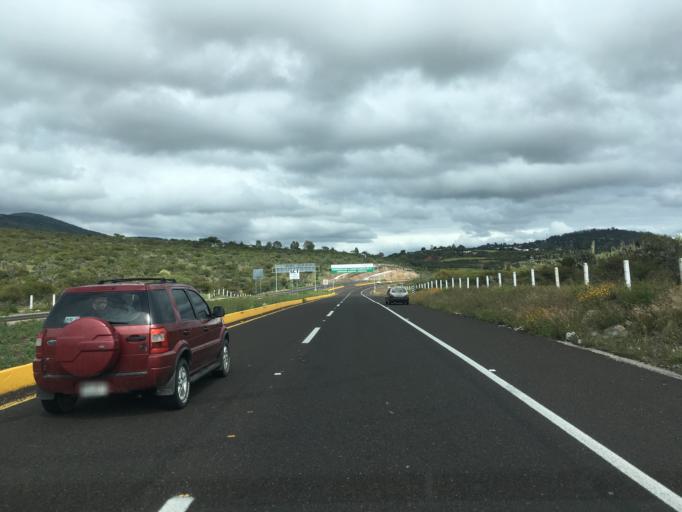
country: MX
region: Hidalgo
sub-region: Atotonilco el Grande
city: Santa Maria Amajac
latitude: 20.3861
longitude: -98.7235
